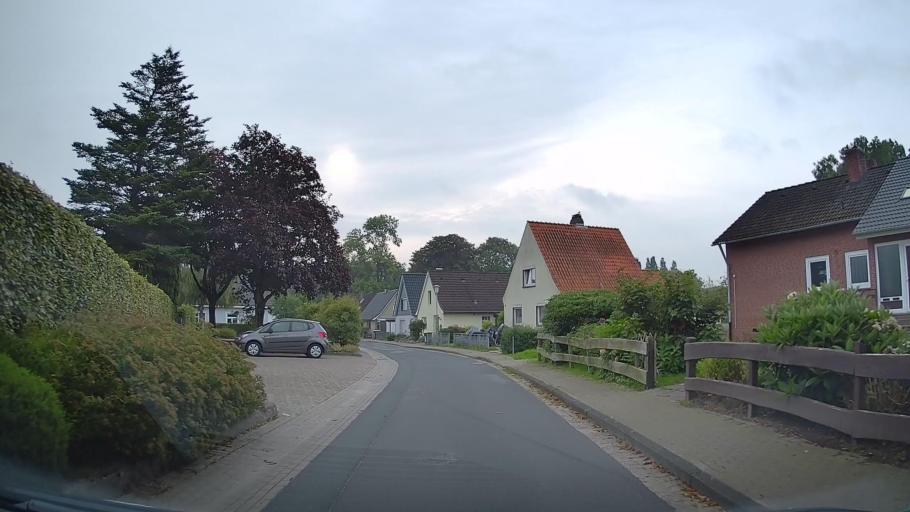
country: DE
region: Lower Saxony
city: Wanna
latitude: 53.8264
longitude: 8.7696
